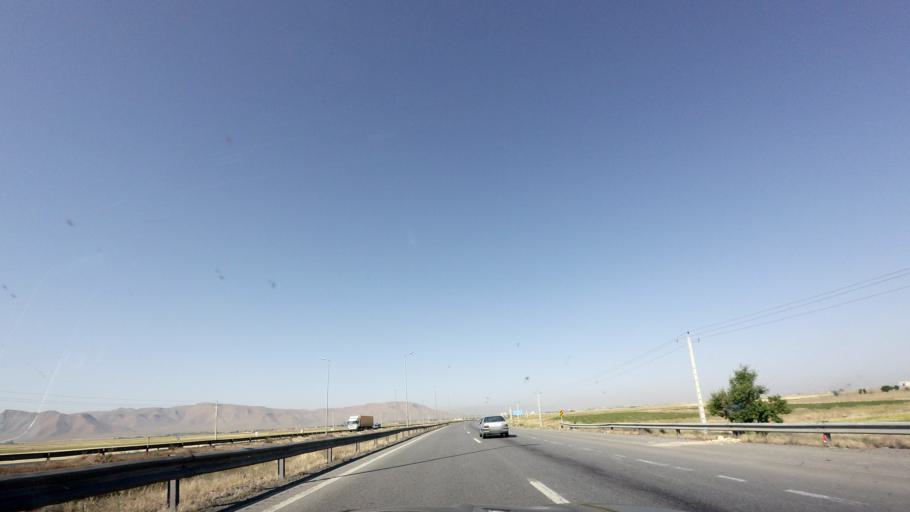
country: IR
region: Markazi
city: Arak
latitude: 34.1667
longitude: 50.0300
